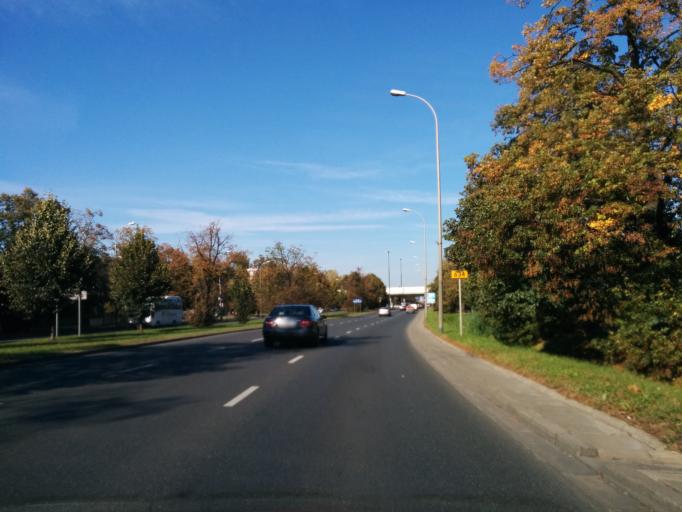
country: PL
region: Masovian Voivodeship
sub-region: Warszawa
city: Wlochy
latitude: 52.1811
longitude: 20.9782
